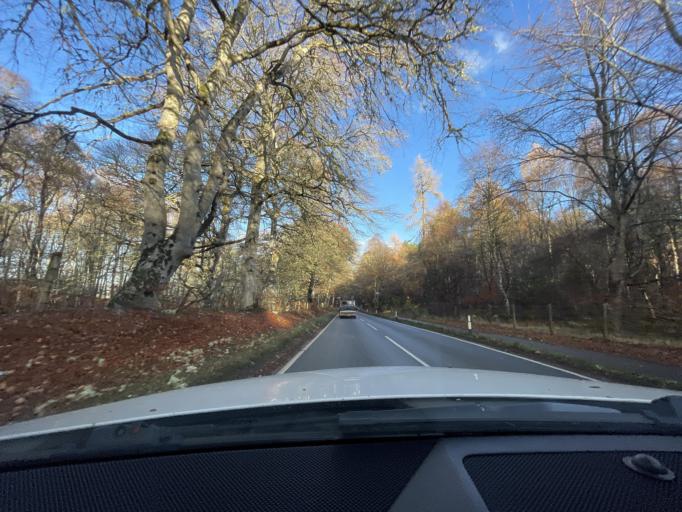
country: GB
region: Scotland
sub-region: Highland
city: Inverness
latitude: 57.4368
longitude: -4.2678
